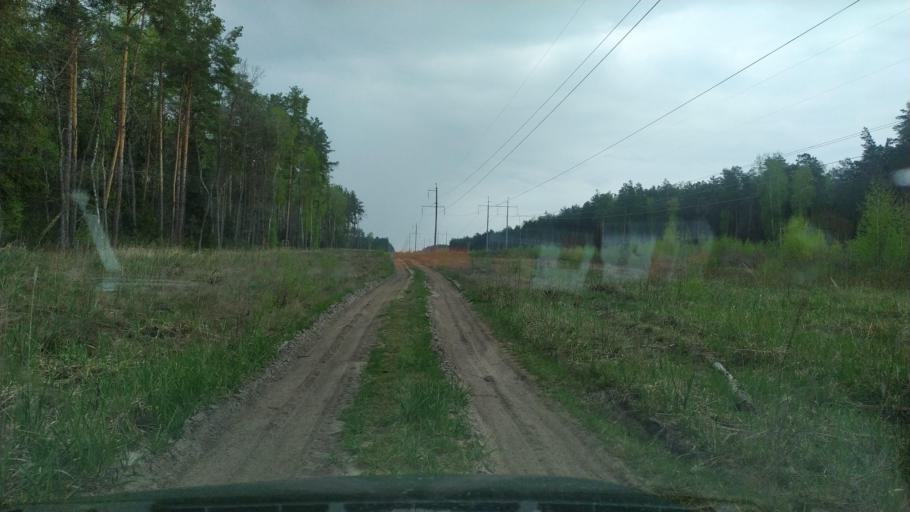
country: BY
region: Brest
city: Pruzhany
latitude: 52.3589
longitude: 24.5874
